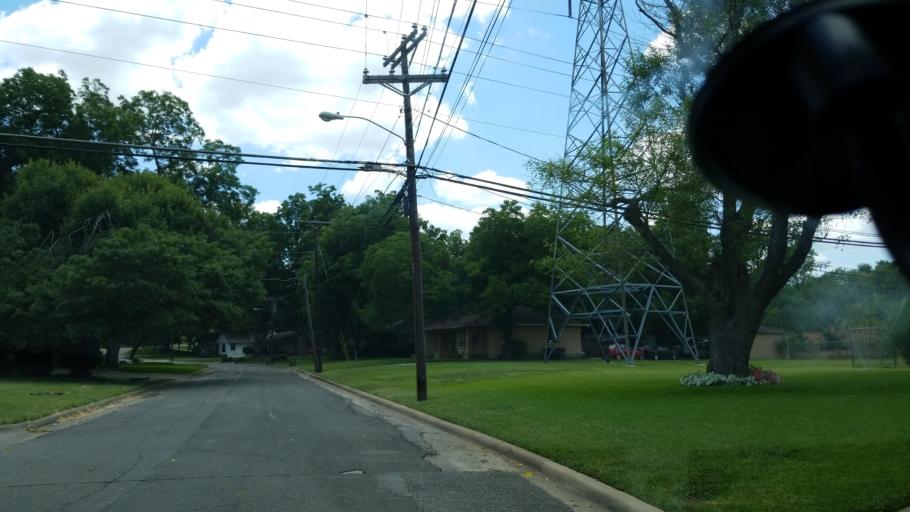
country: US
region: Texas
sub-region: Dallas County
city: Cockrell Hill
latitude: 32.6998
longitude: -96.8551
